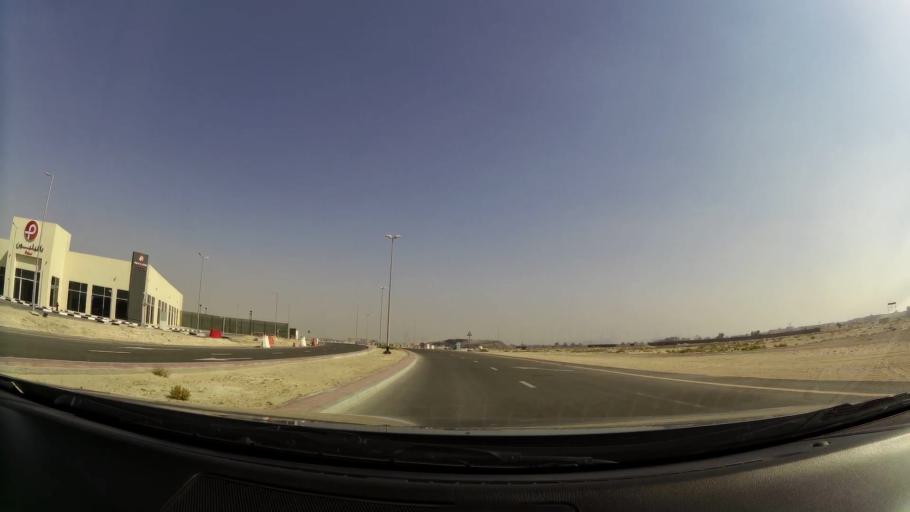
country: AE
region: Dubai
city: Dubai
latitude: 24.9518
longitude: 55.0511
